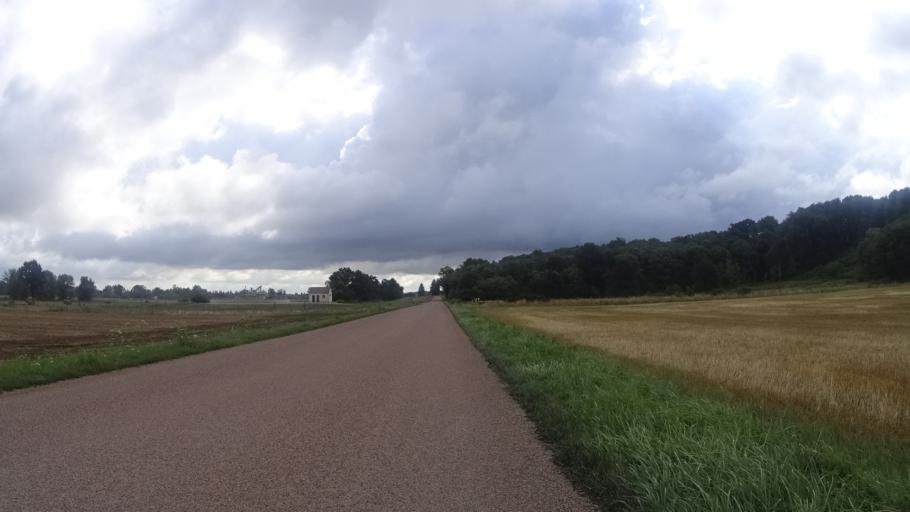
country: FR
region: Bourgogne
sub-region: Departement de l'Yonne
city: Vergigny
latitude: 47.9654
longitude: 3.6759
